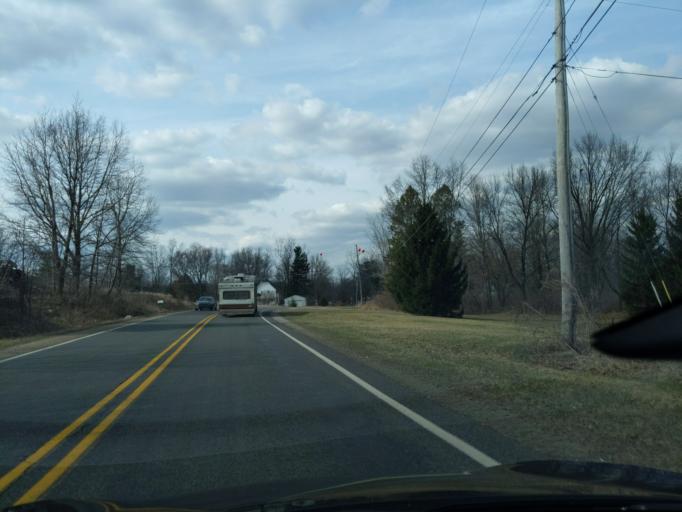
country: US
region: Michigan
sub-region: Ingham County
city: Leslie
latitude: 42.3629
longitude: -84.4203
